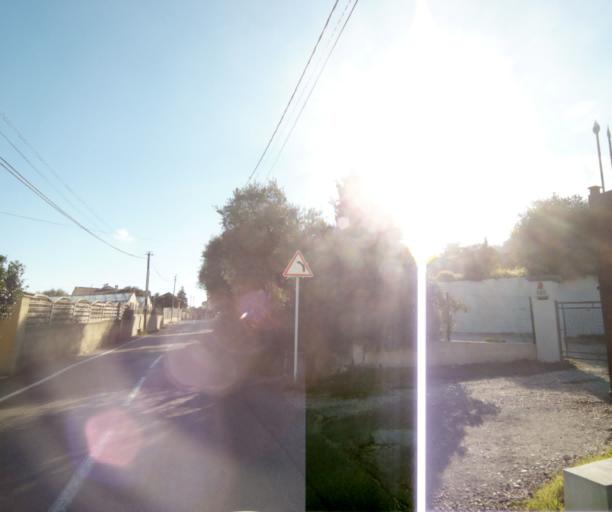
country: FR
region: Provence-Alpes-Cote d'Azur
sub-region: Departement des Alpes-Maritimes
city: Biot
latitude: 43.6034
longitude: 7.1079
